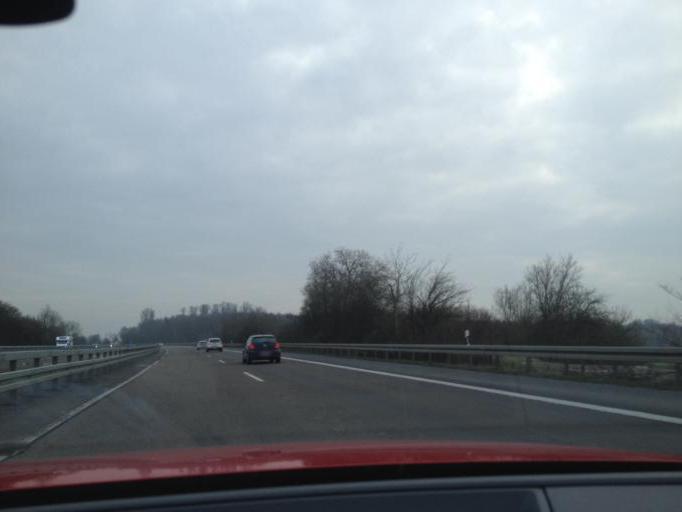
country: DE
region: Hesse
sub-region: Regierungsbezirk Darmstadt
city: Hammersbach
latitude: 50.2152
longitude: 9.0005
